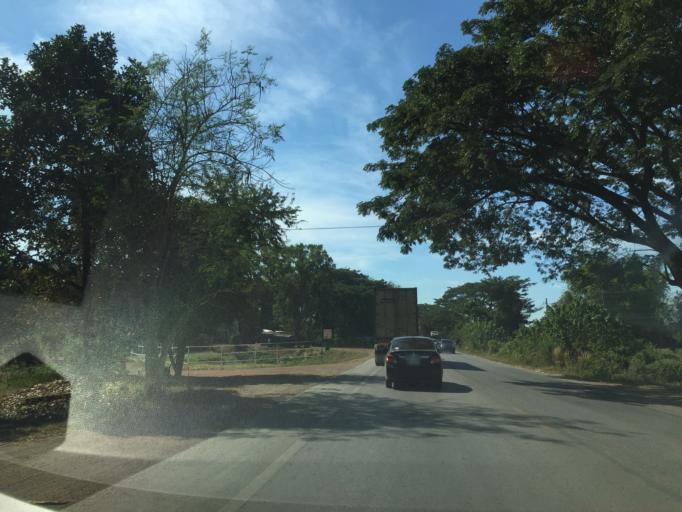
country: TH
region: Changwat Nong Bua Lamphu
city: Na Wang
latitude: 17.3215
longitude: 102.1144
